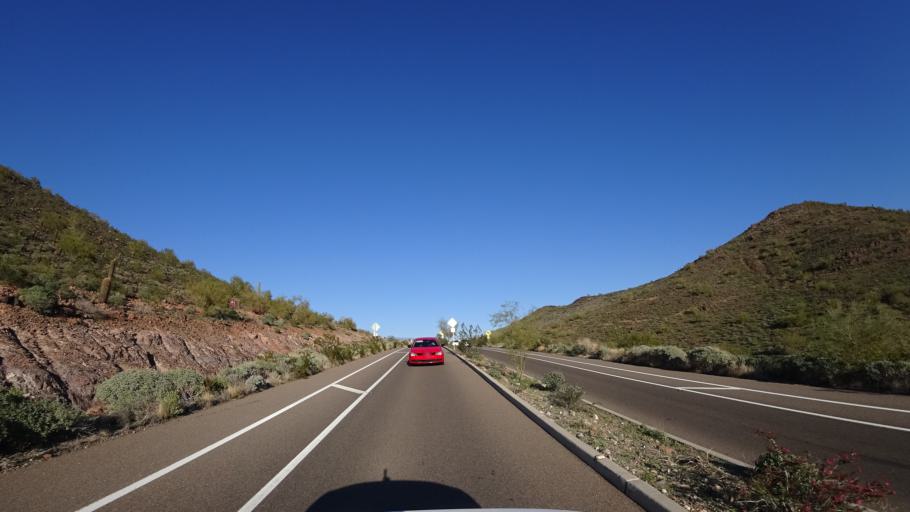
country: US
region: Arizona
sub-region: Maricopa County
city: Peoria
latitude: 33.6916
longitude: -112.1867
